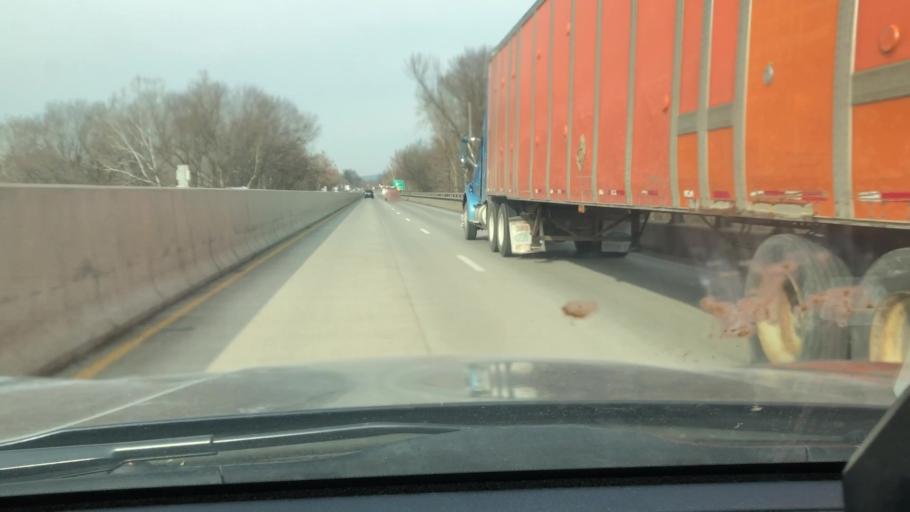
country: US
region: Pennsylvania
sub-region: Chester County
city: South Pottstown
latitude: 40.2418
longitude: -75.6593
